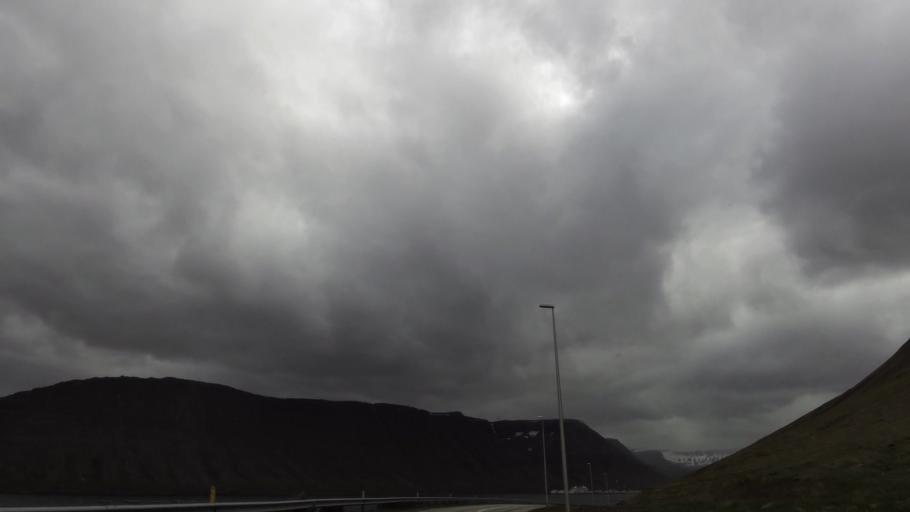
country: IS
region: Westfjords
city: Isafjoerdur
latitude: 66.1003
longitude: -23.1094
